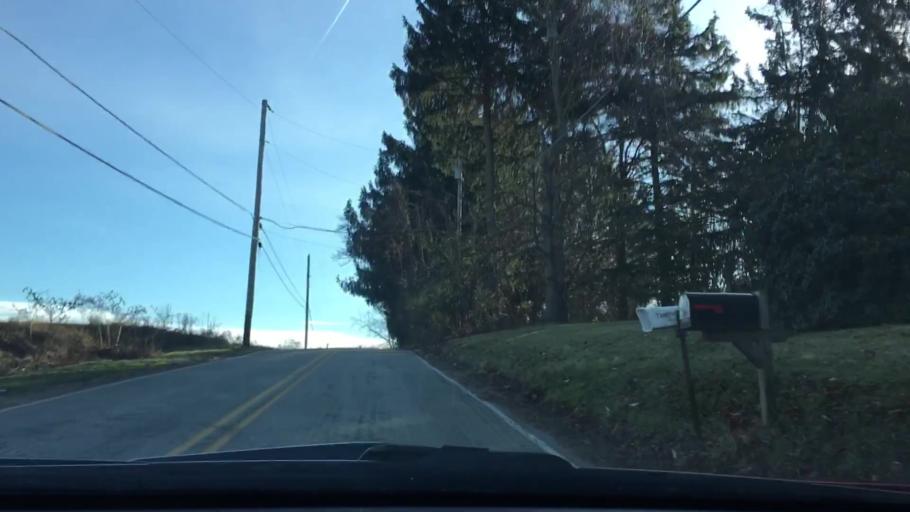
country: US
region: Pennsylvania
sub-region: Westmoreland County
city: Irwin
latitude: 40.3006
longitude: -79.6982
